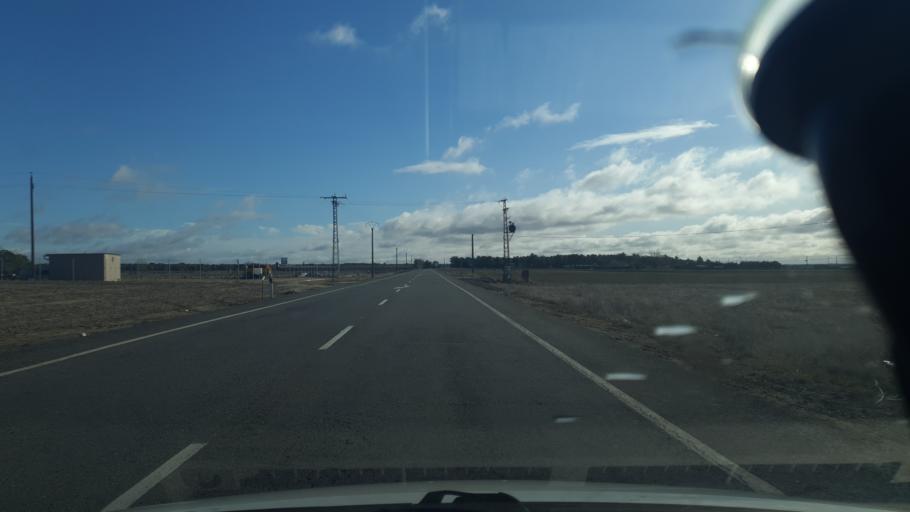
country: ES
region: Castille and Leon
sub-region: Provincia de Segovia
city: Martin Munoz de la Dehesa
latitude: 41.0478
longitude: -4.6917
